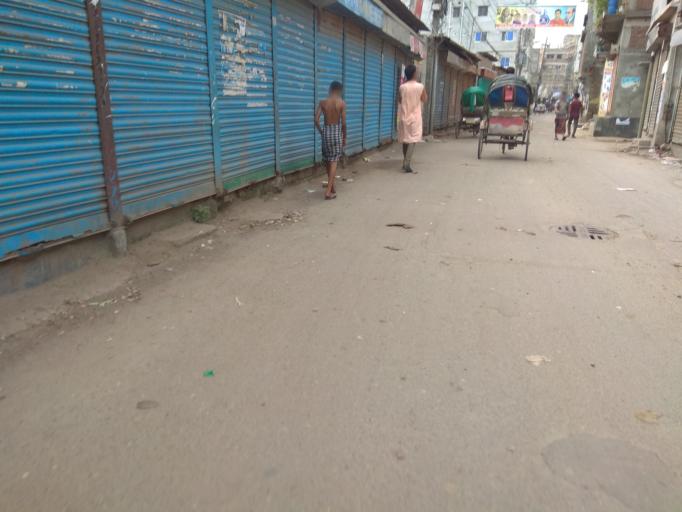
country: BD
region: Dhaka
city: Azimpur
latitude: 23.7132
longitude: 90.3786
